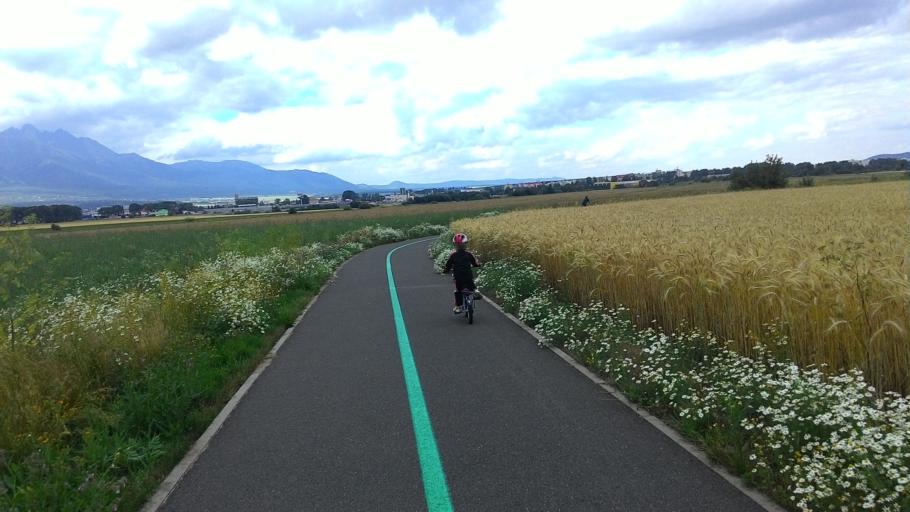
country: SK
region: Presovsky
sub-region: Okres Poprad
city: Poprad
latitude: 49.0428
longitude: 20.2718
